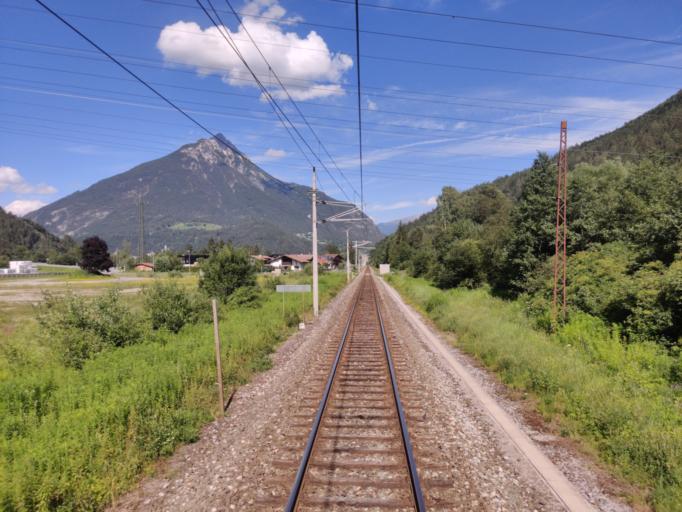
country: AT
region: Tyrol
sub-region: Politischer Bezirk Imst
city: Imsterberg
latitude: 47.2131
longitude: 10.7183
